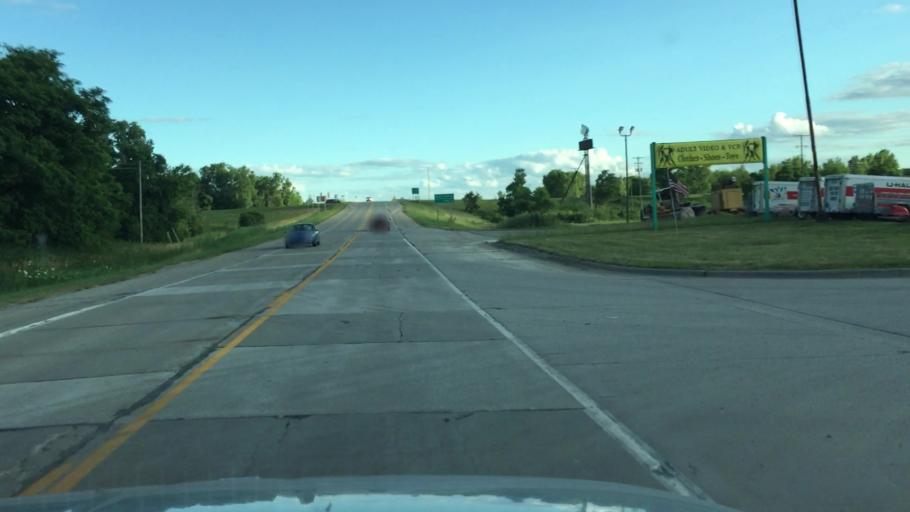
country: US
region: Michigan
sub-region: Macomb County
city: Memphis
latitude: 42.9850
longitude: -82.7648
